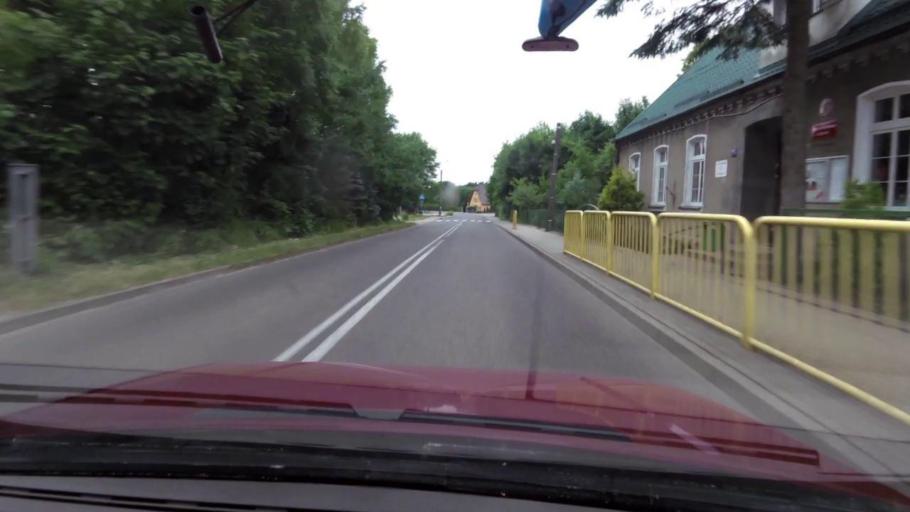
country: PL
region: West Pomeranian Voivodeship
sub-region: Powiat koszalinski
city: Sianow
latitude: 54.1806
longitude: 16.3819
